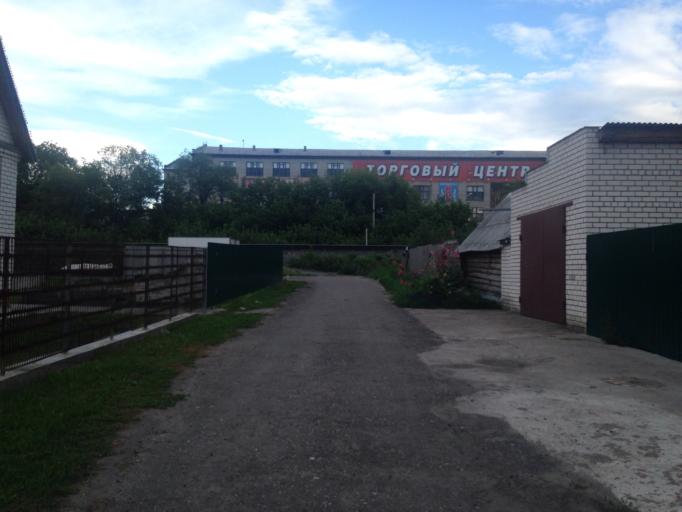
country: RU
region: Ulyanovsk
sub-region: Ulyanovskiy Rayon
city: Ulyanovsk
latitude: 54.2445
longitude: 48.3096
